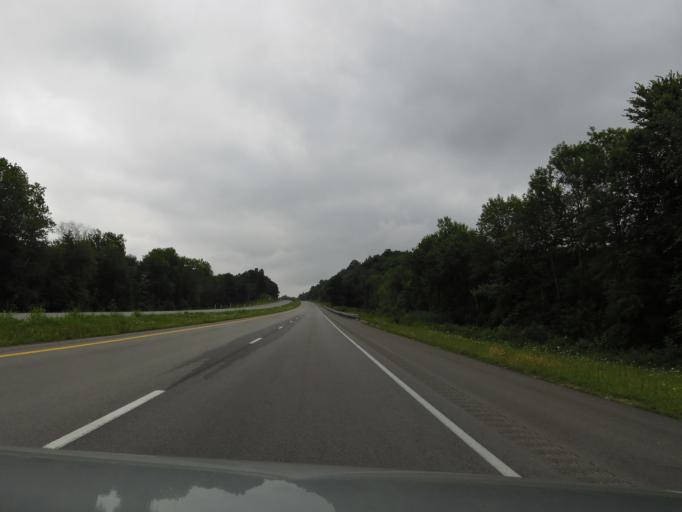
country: US
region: Kentucky
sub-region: Grayson County
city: Leitchfield
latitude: 37.4124
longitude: -86.4269
